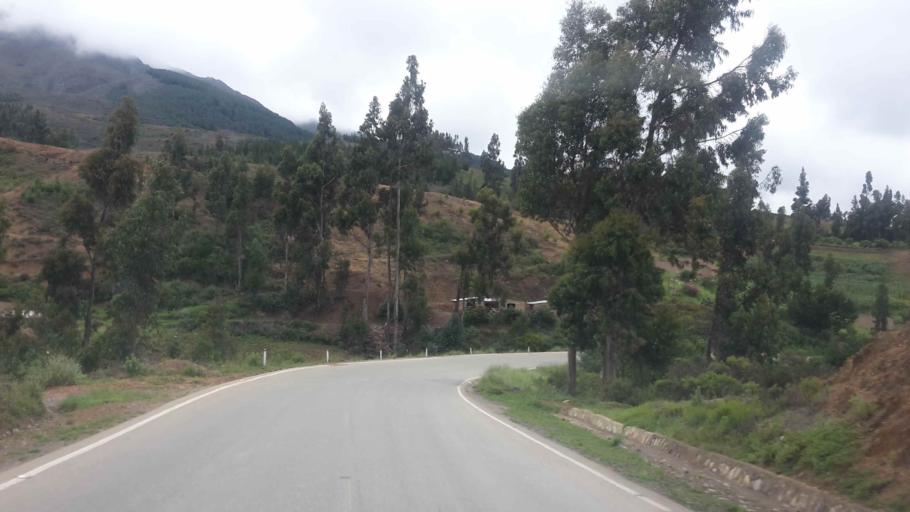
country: BO
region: Cochabamba
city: Totora
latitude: -17.5700
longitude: -65.3187
